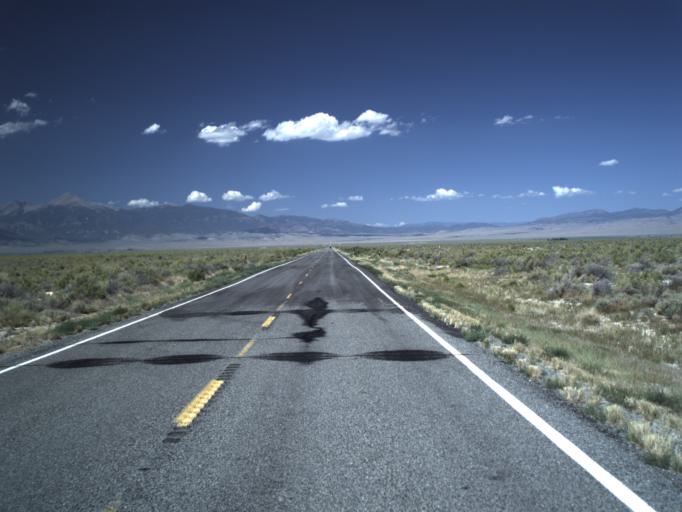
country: US
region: Nevada
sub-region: White Pine County
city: McGill
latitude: 39.0458
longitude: -113.9013
